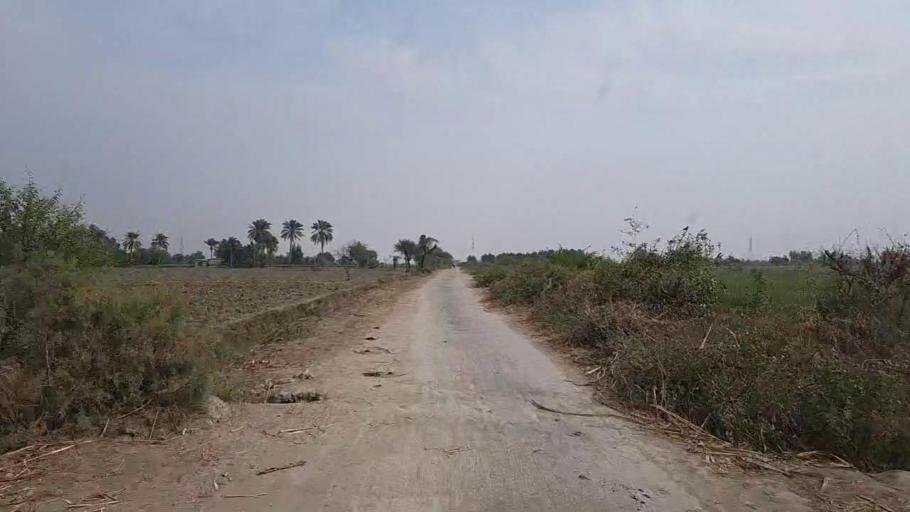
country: PK
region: Sindh
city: Mirwah Gorchani
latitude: 25.3573
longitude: 69.0315
